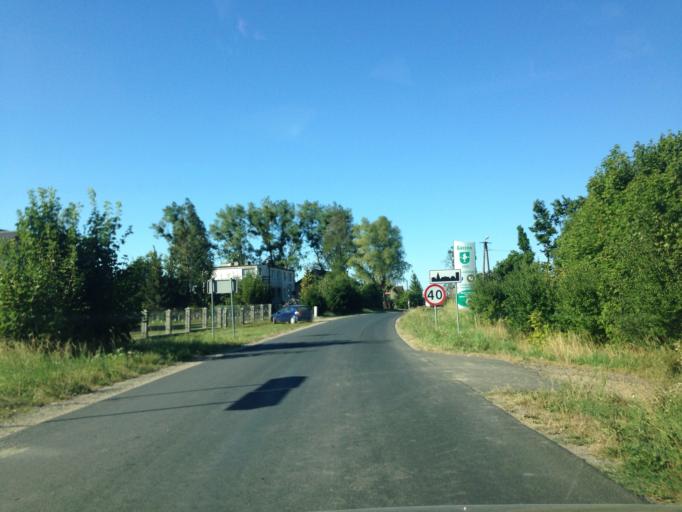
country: PL
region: Kujawsko-Pomorskie
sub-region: Powiat brodnicki
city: Gorzno
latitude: 53.1876
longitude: 19.6391
